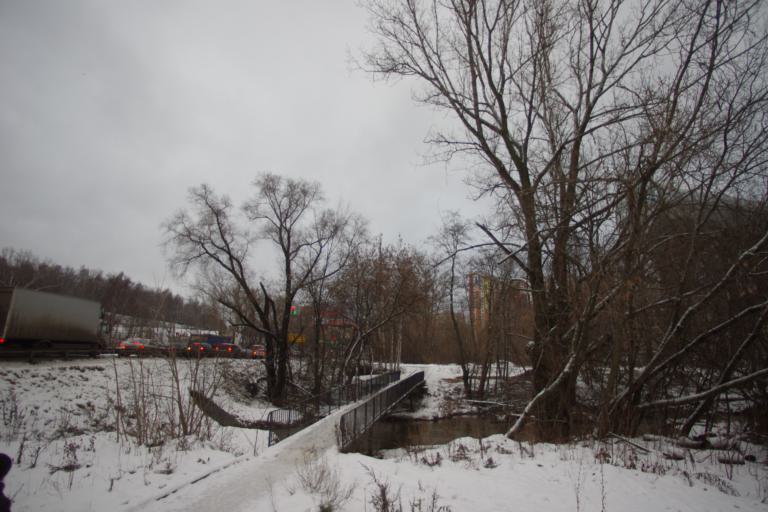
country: RU
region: Moskovskaya
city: Pavshino
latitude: 55.8165
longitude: 37.3565
